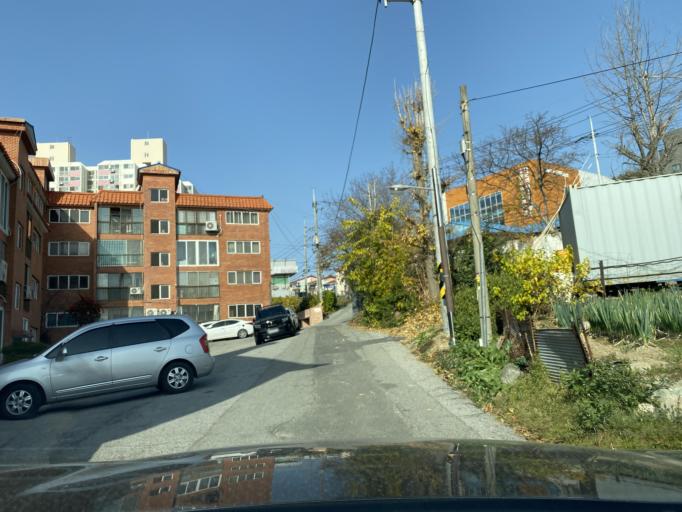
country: KR
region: Chungcheongnam-do
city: Yesan
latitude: 36.6851
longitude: 126.8456
